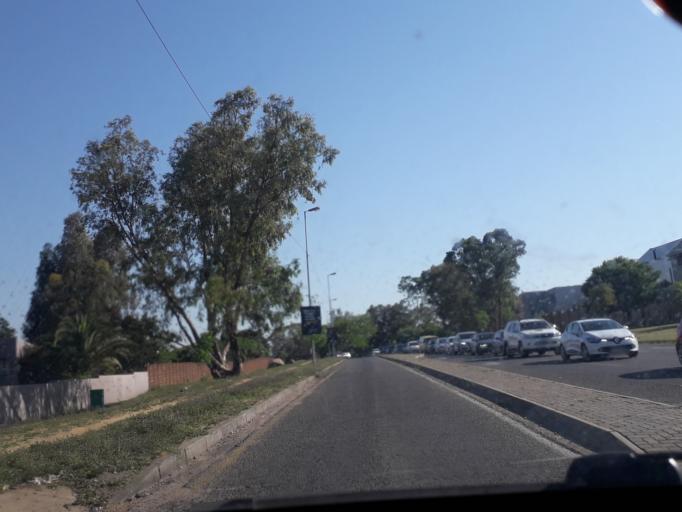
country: ZA
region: Gauteng
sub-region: City of Johannesburg Metropolitan Municipality
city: Midrand
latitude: -26.0524
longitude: 28.0711
